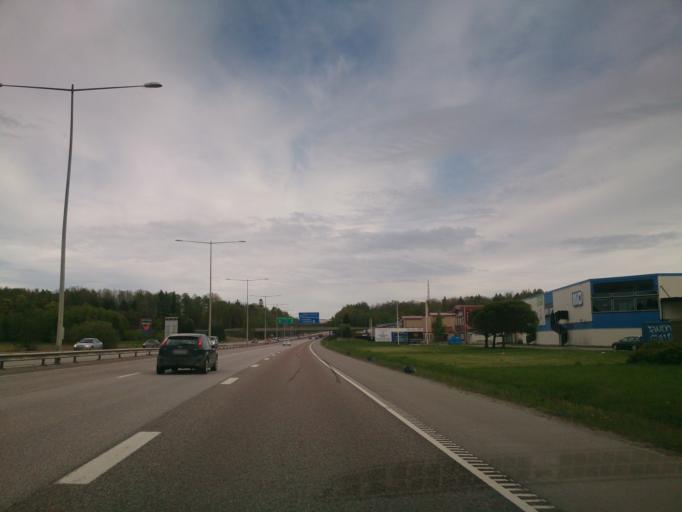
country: SE
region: Stockholm
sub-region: Haninge Kommun
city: Haninge
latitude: 59.1874
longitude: 18.1478
